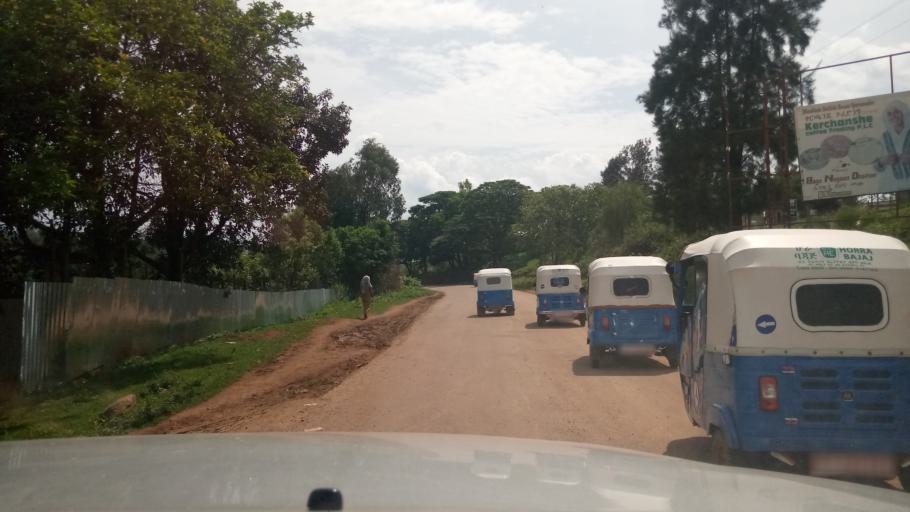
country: ET
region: Oromiya
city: Agaro
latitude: 7.8535
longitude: 36.5956
